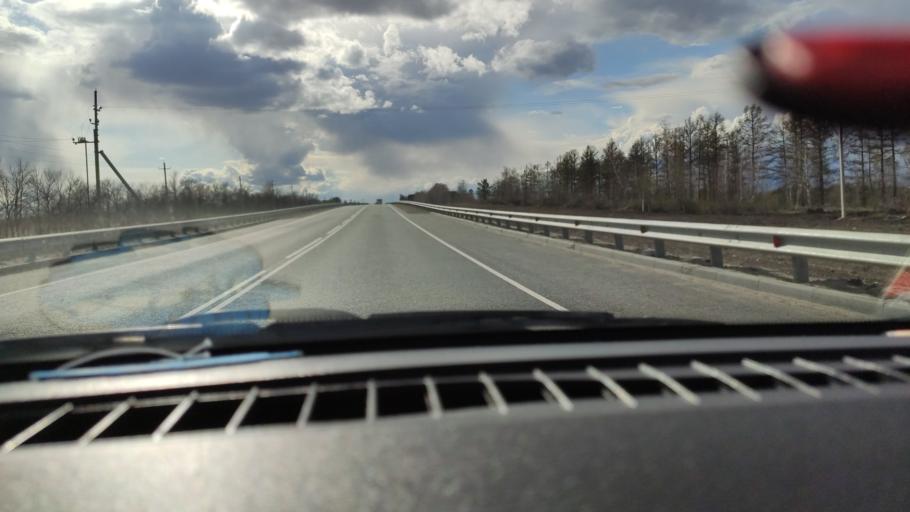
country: RU
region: Saratov
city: Shikhany
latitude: 52.1609
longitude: 47.1242
